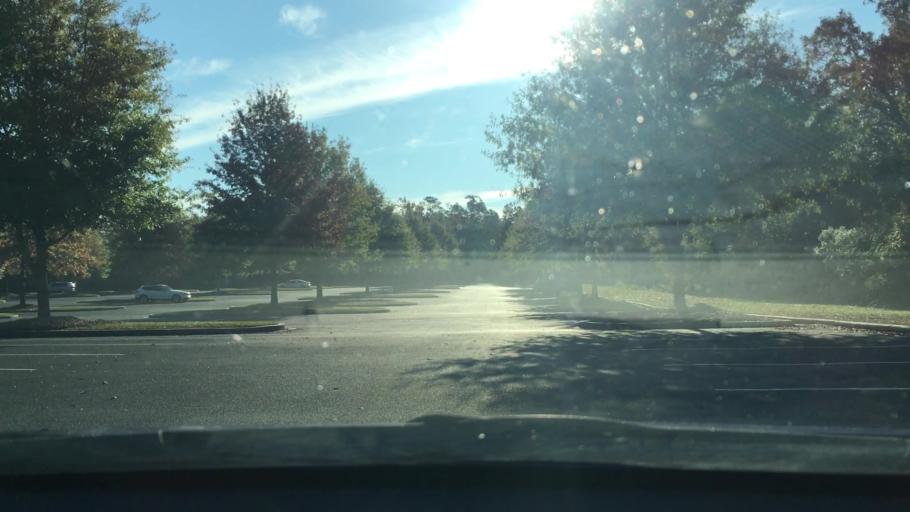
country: US
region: South Carolina
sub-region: Lexington County
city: Irmo
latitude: 34.0845
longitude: -81.1533
